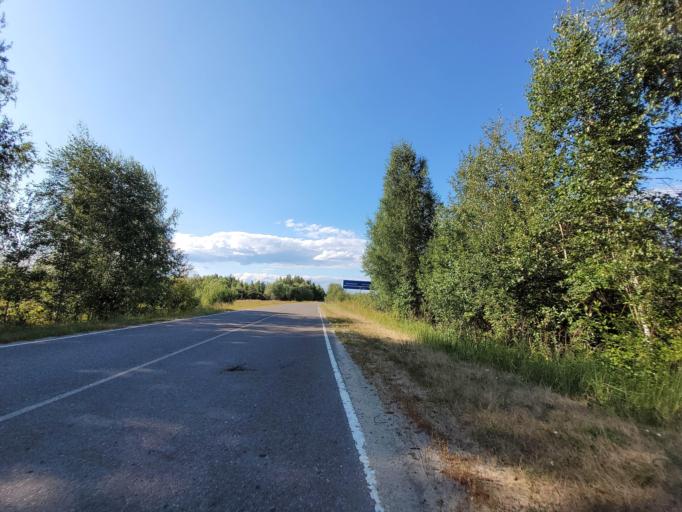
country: RU
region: Moskovskaya
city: Konobeyevo
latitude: 55.4014
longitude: 38.7094
